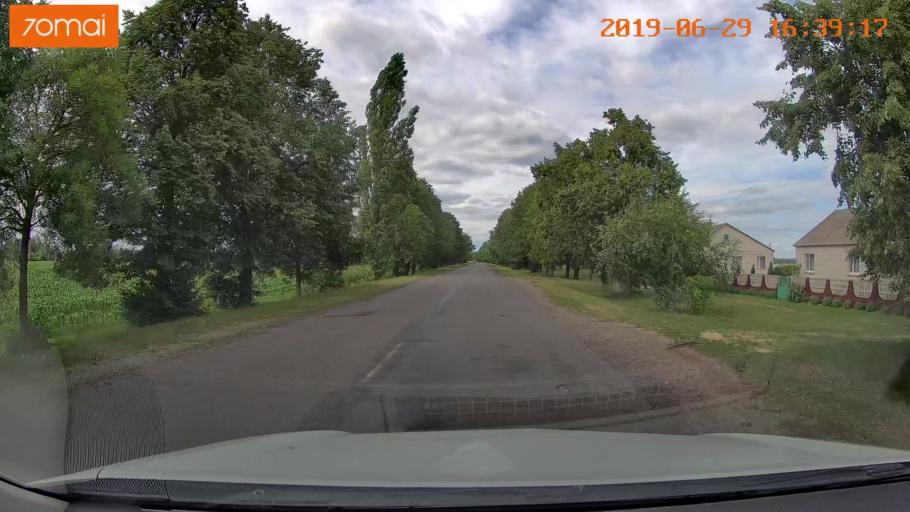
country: BY
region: Brest
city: Luninyets
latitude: 52.2406
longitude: 27.0159
